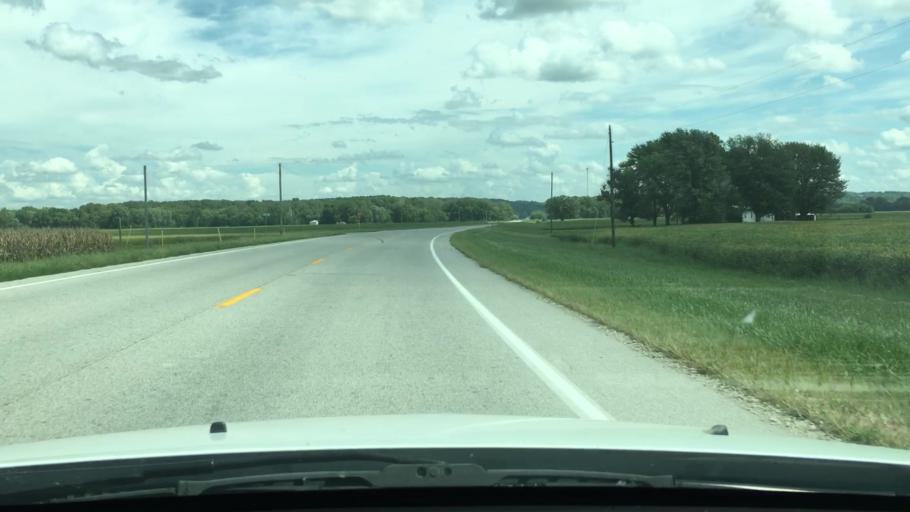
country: US
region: Missouri
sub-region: Pike County
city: Louisiana
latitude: 39.4983
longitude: -90.9999
